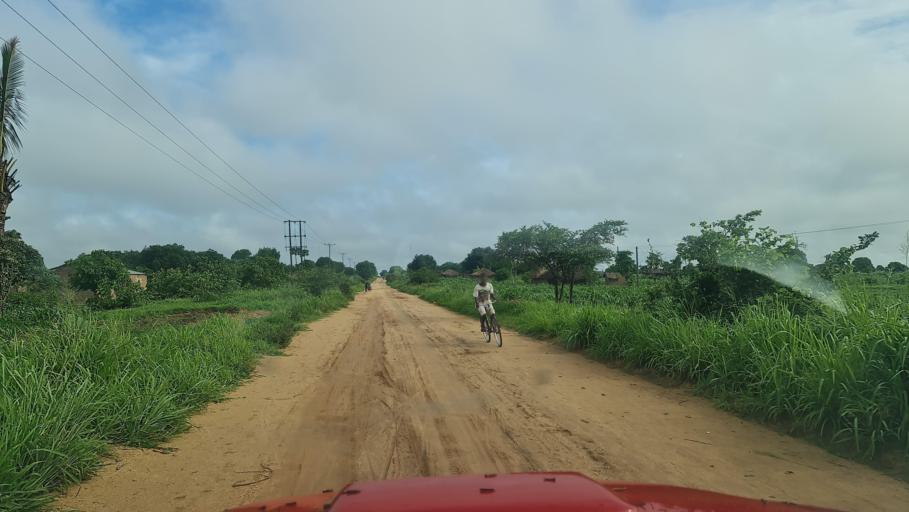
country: MW
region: Southern Region
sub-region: Nsanje District
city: Nsanje
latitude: -17.3092
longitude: 35.5929
